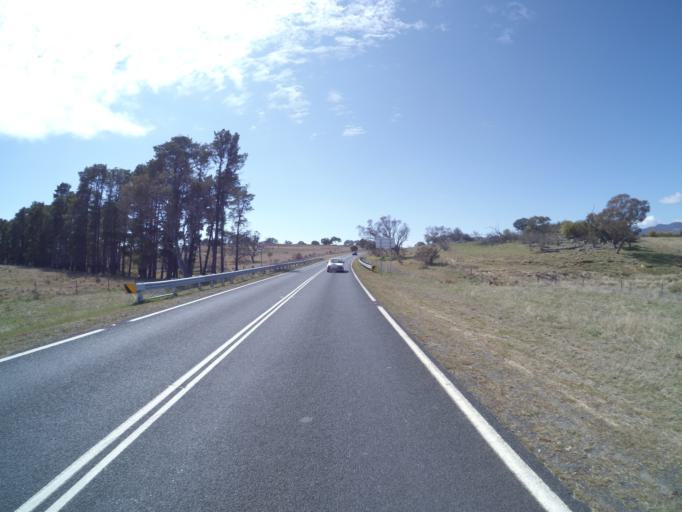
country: AU
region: Australian Capital Territory
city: Macarthur
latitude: -35.4480
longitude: 149.0562
